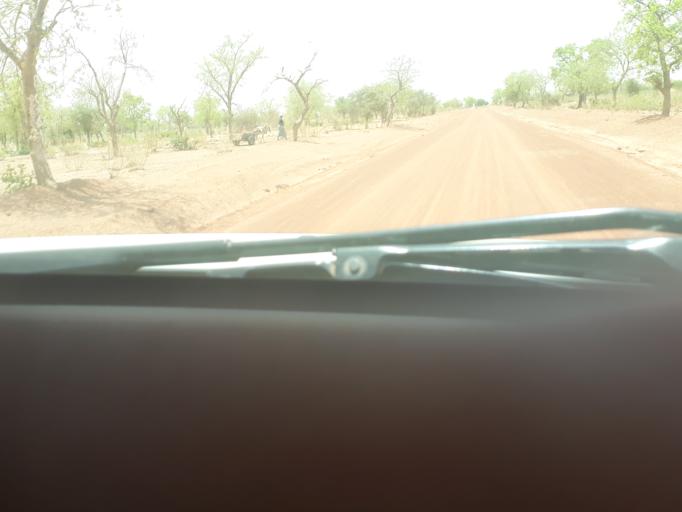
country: BF
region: Plateau-Central
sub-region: Province d'Oubritenga
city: Ziniare
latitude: 12.5799
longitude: -1.3359
